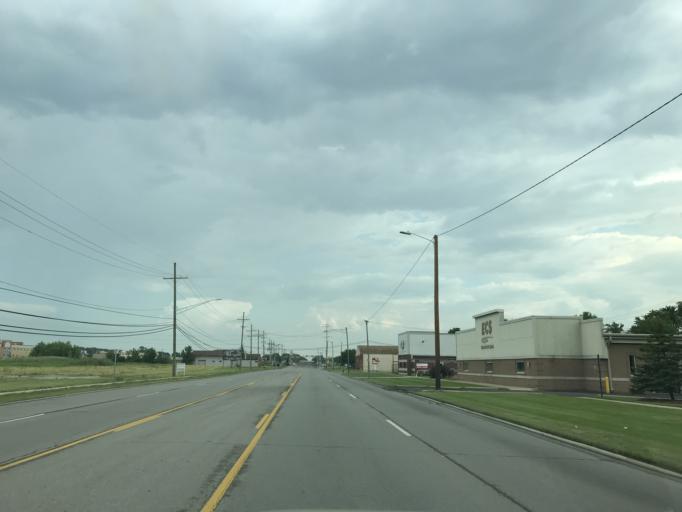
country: US
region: Michigan
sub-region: Wayne County
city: Southgate
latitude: 42.2166
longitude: -83.2294
